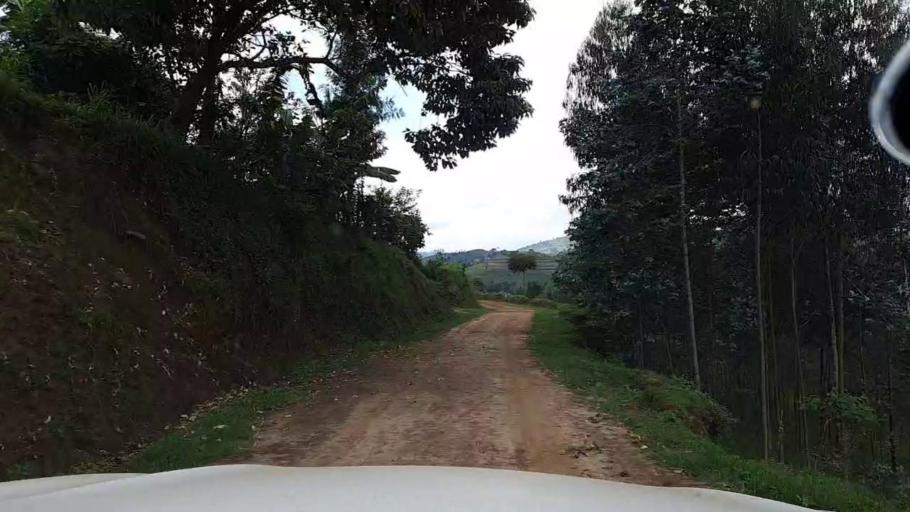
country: RW
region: Southern Province
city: Nzega
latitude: -2.6379
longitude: 29.4829
